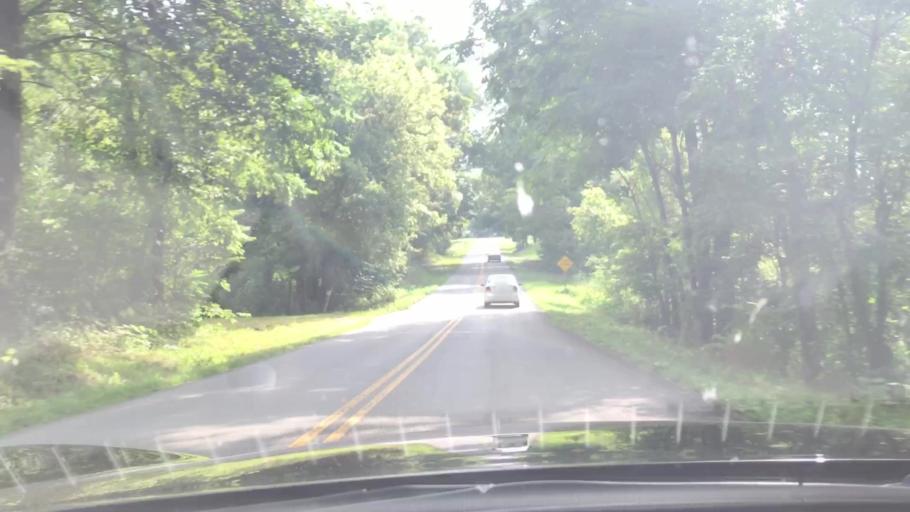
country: US
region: Kentucky
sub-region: Green County
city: Greensburg
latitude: 37.2682
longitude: -85.5398
